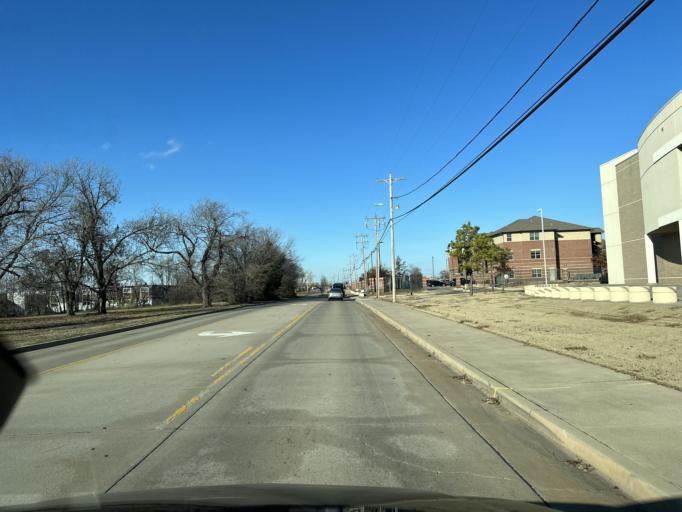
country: US
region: Oklahoma
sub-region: Oklahoma County
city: Midwest City
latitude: 35.4457
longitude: -97.4164
